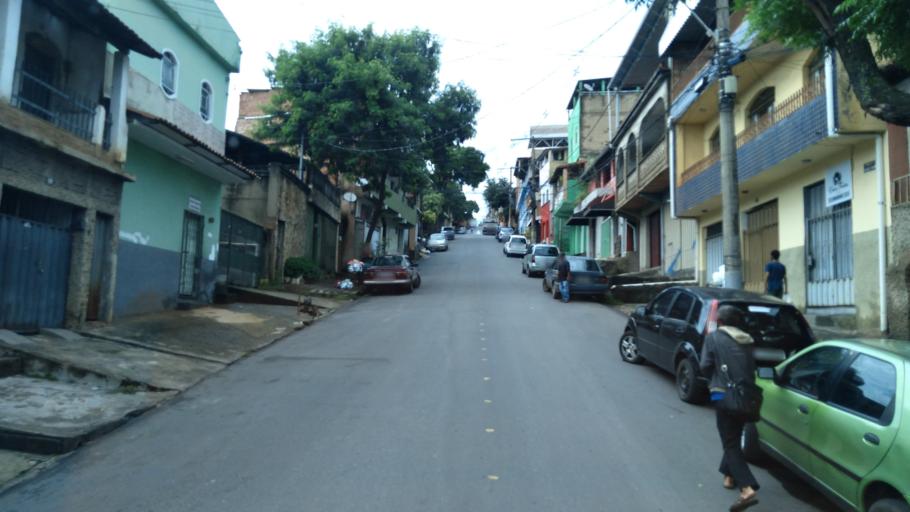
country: BR
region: Minas Gerais
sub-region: Belo Horizonte
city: Belo Horizonte
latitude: -19.9046
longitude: -43.8926
